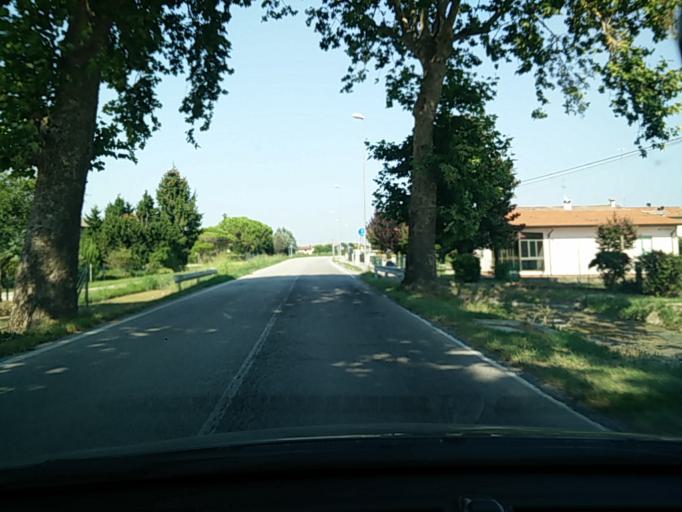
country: IT
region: Veneto
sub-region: Provincia di Venezia
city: Crepaldo
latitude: 45.6119
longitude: 12.7138
